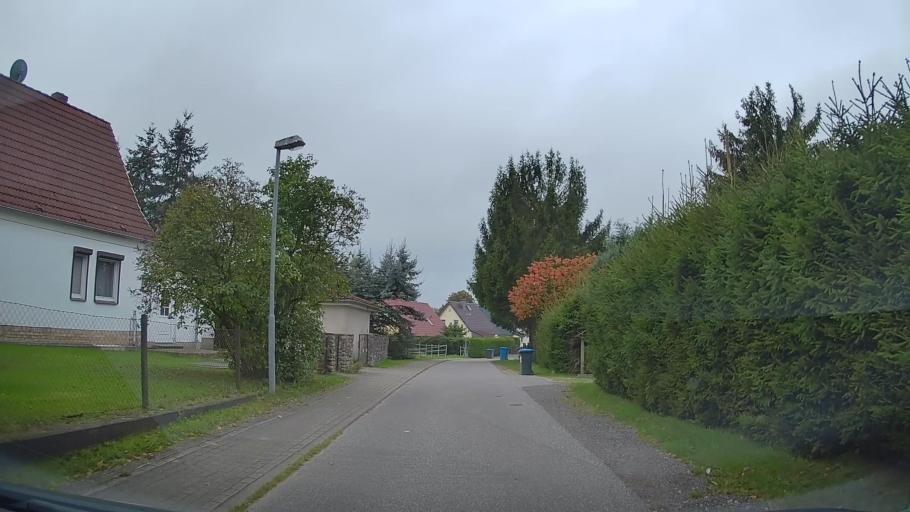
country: DE
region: Mecklenburg-Vorpommern
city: Guestrow
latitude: 53.8453
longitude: 12.1735
